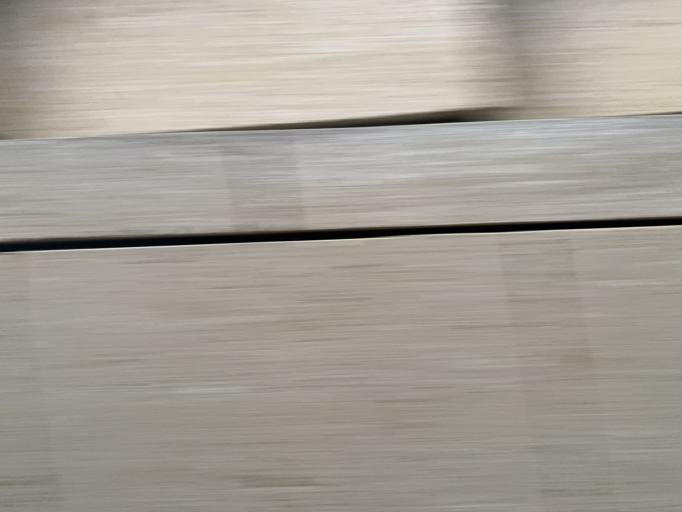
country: FR
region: Rhone-Alpes
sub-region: Departement du Rhone
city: Meyzieu
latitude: 45.7703
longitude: 5.0101
